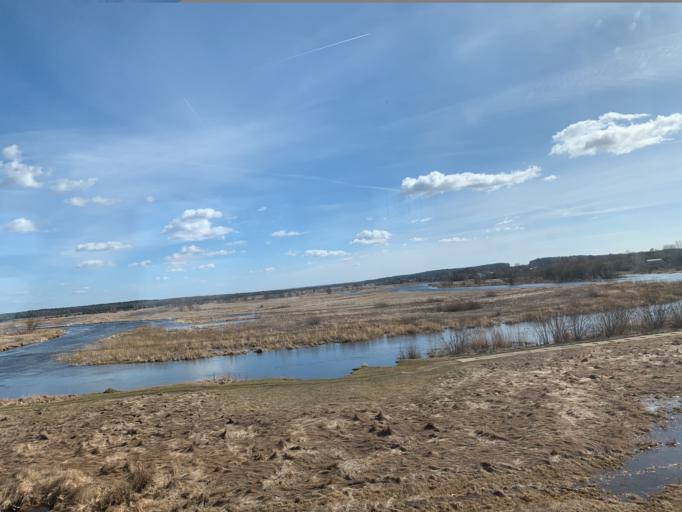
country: BY
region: Minsk
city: Novy Svyerzhan'
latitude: 53.4655
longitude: 26.7281
